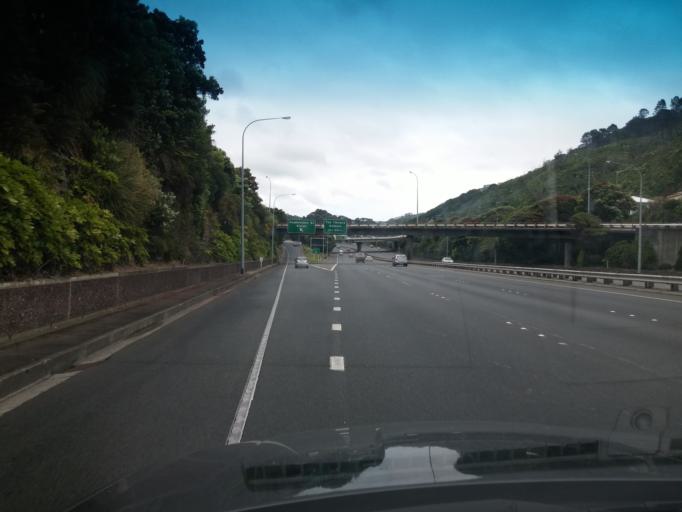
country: NZ
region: Wellington
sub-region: Wellington City
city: Wellington
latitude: -41.2724
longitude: 174.7776
